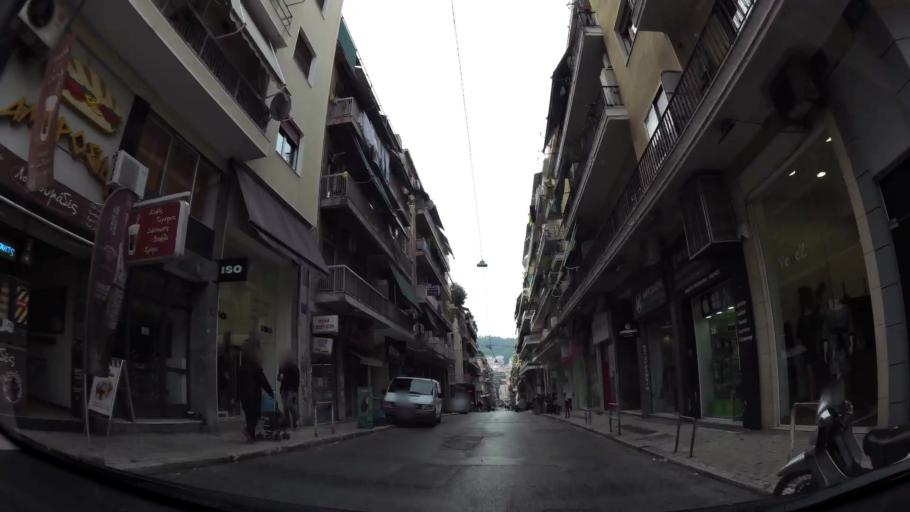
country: GR
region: Attica
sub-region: Nomarchia Athinas
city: Kipseli
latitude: 37.9921
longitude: 23.7487
